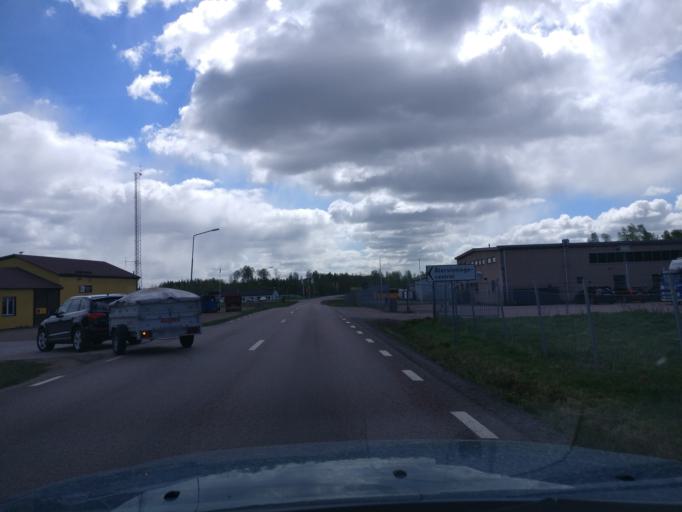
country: SE
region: Vaermland
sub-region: Karlstads Kommun
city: Molkom
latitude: 59.6078
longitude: 13.7376
